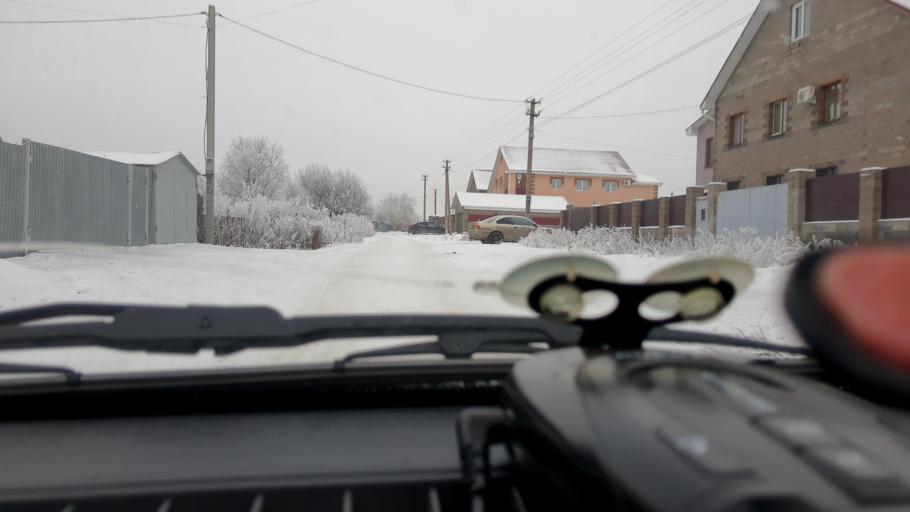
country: RU
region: Bashkortostan
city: Iglino
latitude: 54.7820
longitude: 56.2332
